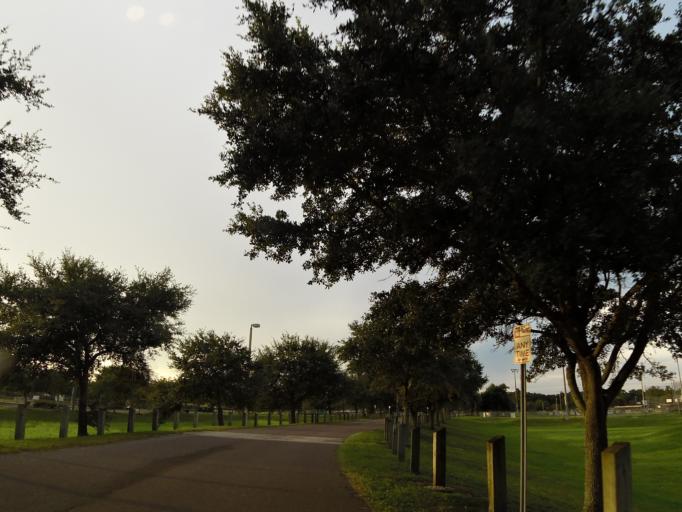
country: US
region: Florida
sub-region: Duval County
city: Atlantic Beach
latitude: 30.3633
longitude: -81.5061
